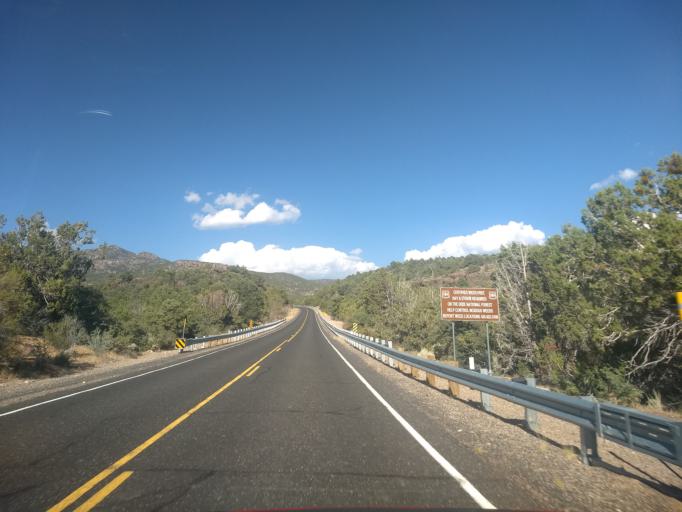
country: US
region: Utah
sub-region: Washington County
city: Enterprise
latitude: 37.4192
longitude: -113.5951
